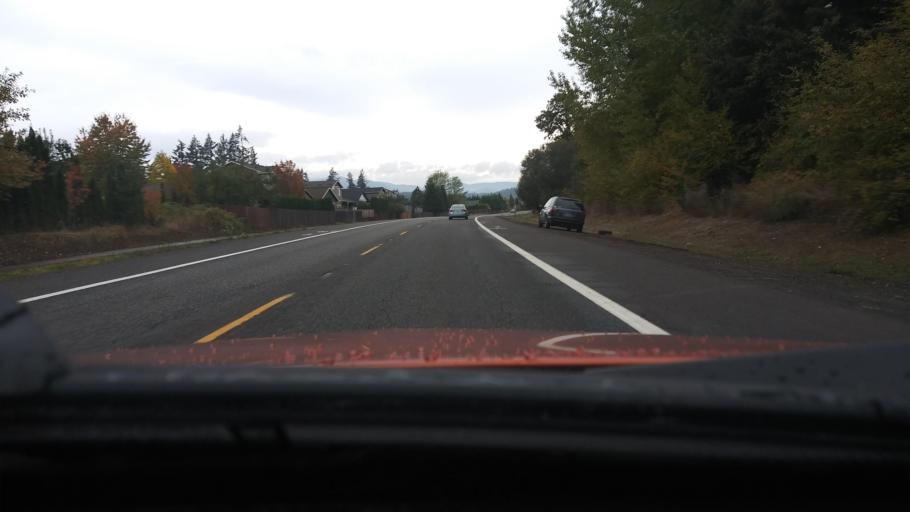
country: US
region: Oregon
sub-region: Washington County
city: Forest Grove
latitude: 45.5302
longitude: -123.0953
